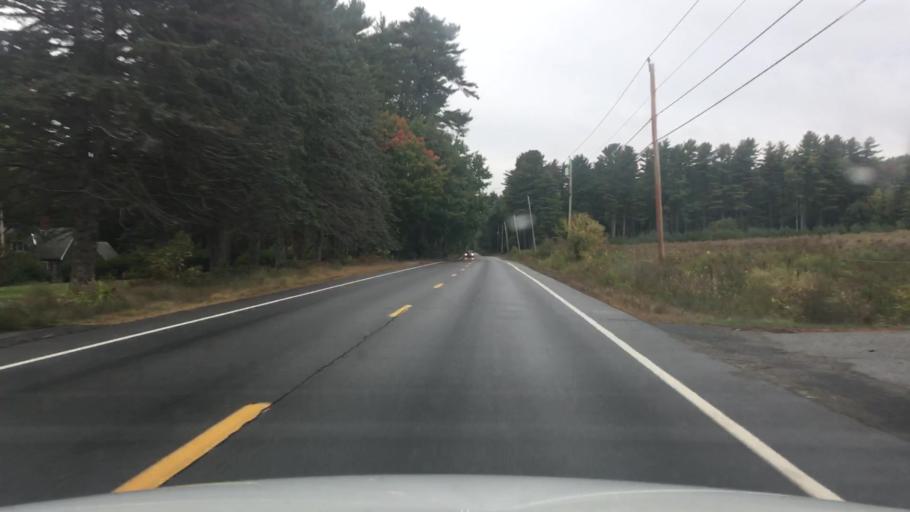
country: US
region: Maine
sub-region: Kennebec County
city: Rome
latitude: 44.5363
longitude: -69.8891
